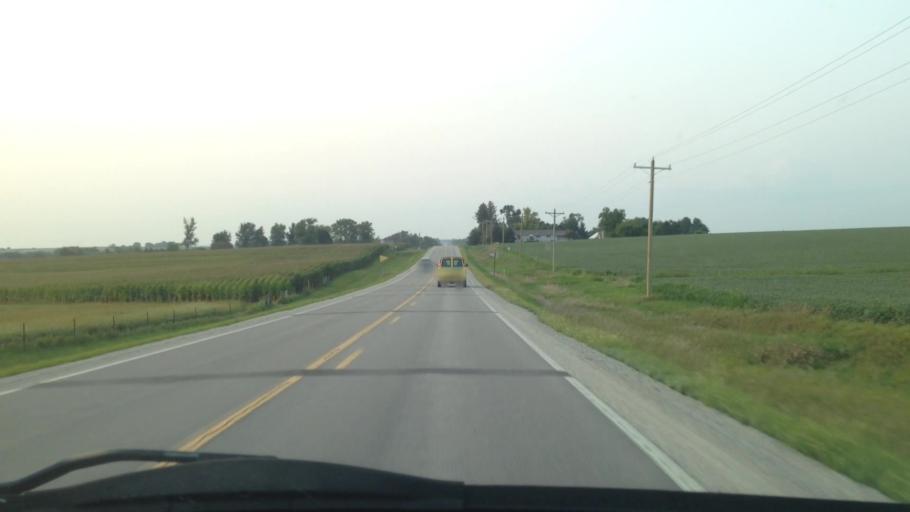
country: US
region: Iowa
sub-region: Benton County
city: Atkins
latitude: 42.0462
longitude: -91.8693
